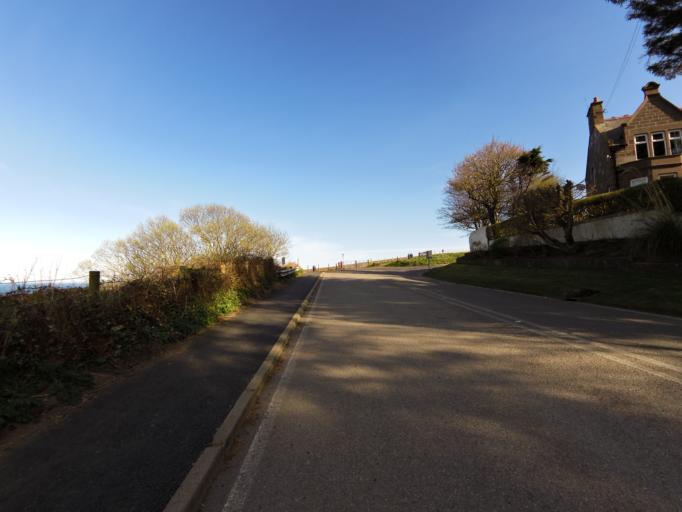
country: GB
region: Scotland
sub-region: Aberdeenshire
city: Stonehaven
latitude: 56.9575
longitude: -2.2030
